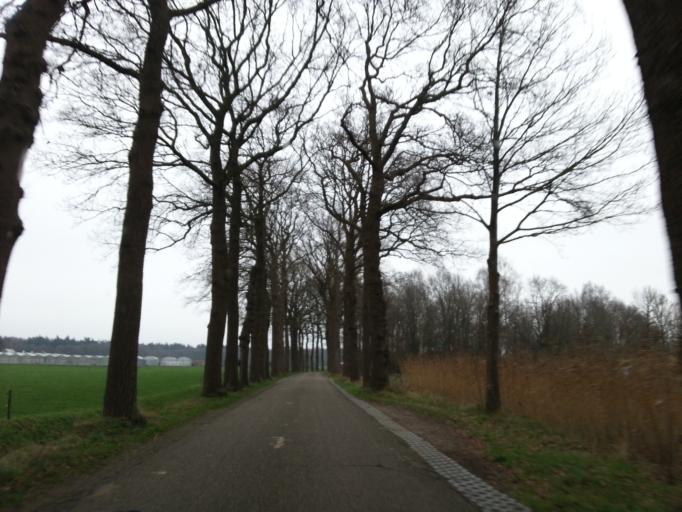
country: NL
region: Overijssel
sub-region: Gemeente Dalfsen
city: Dalfsen
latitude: 52.5167
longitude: 6.2310
